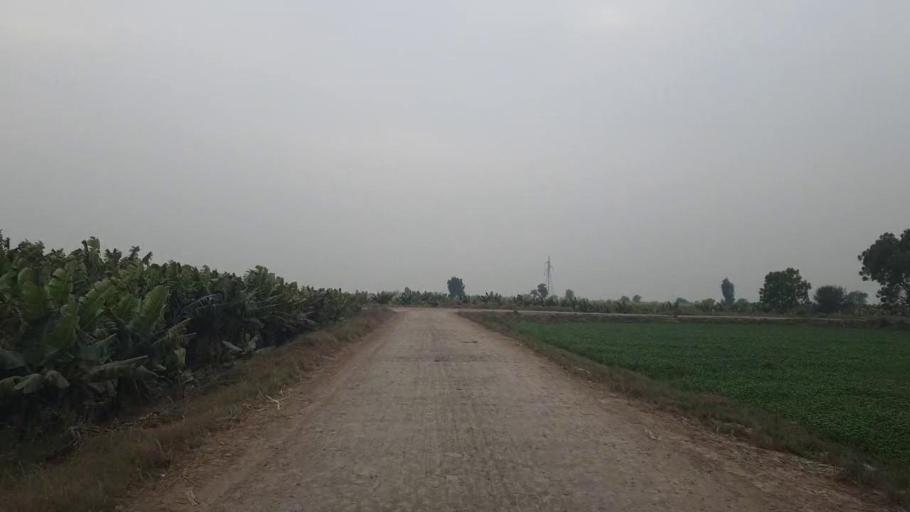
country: PK
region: Sindh
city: Shahdadpur
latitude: 25.8645
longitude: 68.6242
